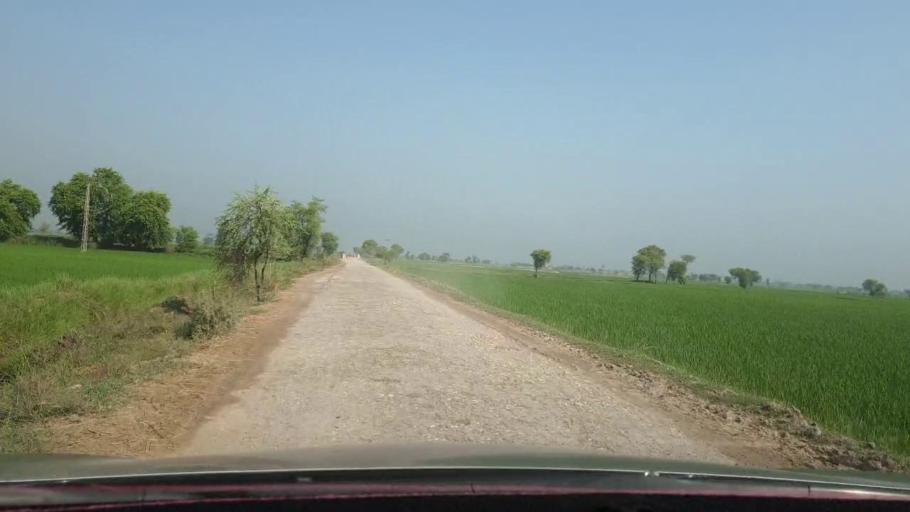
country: PK
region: Sindh
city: Kambar
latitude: 27.5901
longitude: 67.9393
